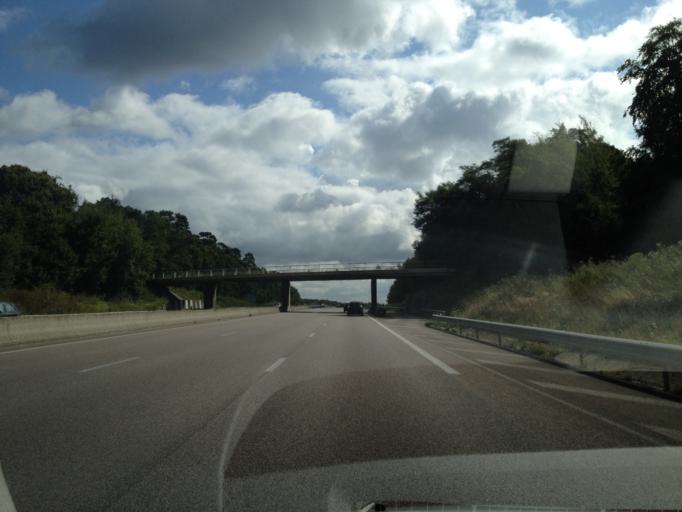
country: FR
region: Haute-Normandie
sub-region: Departement de la Seine-Maritime
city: Cleon
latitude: 49.3424
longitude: 1.0341
